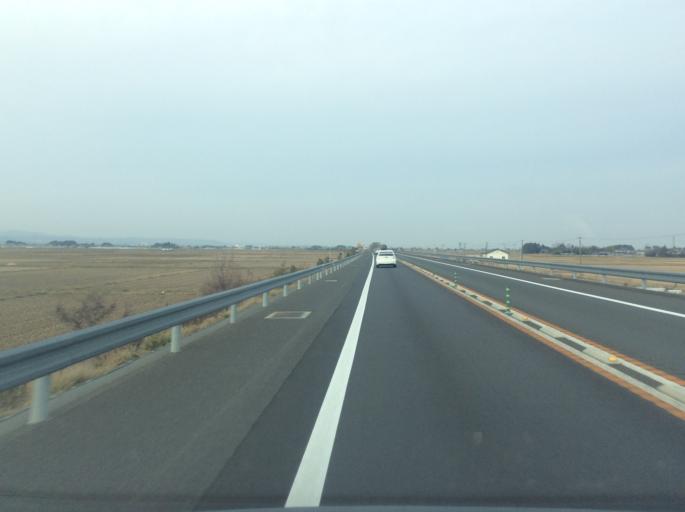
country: JP
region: Miyagi
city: Watari
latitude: 38.0598
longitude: 140.8937
